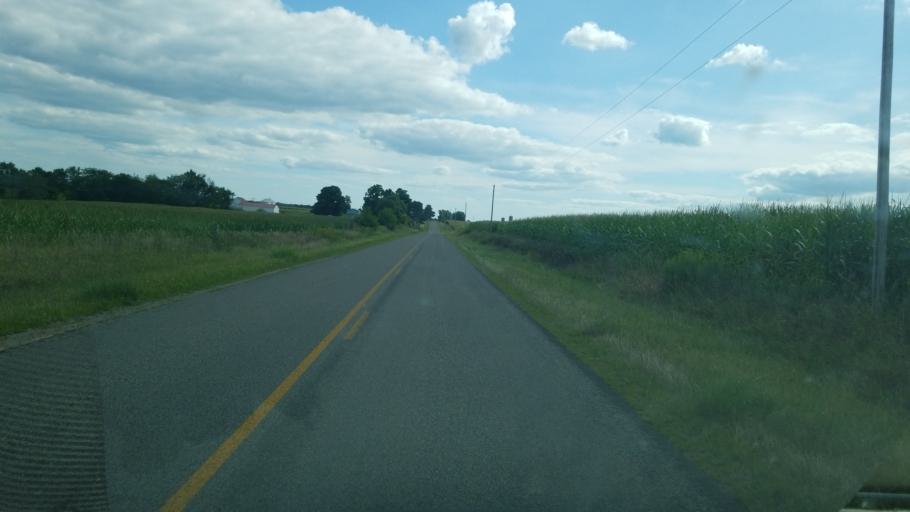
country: US
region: Ohio
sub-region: Logan County
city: De Graff
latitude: 40.2863
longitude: -83.9249
